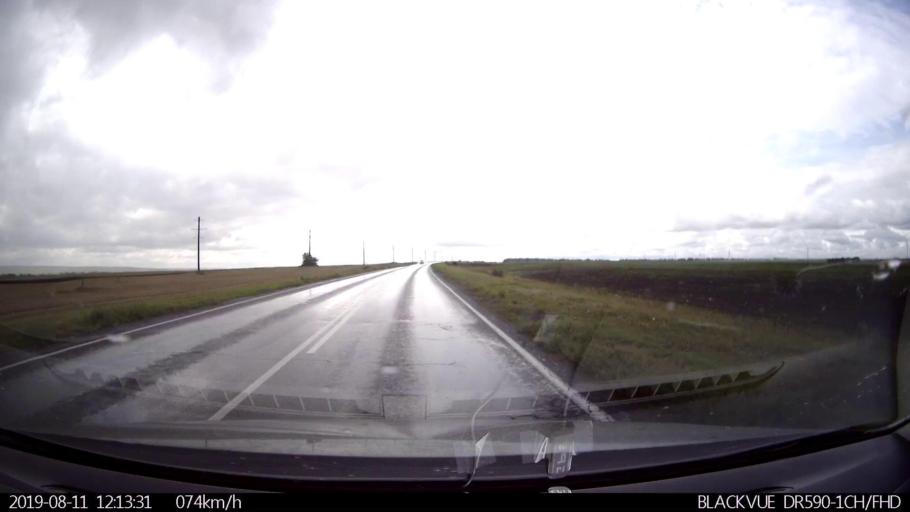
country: RU
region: Ulyanovsk
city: Silikatnyy
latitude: 53.9611
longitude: 47.9915
